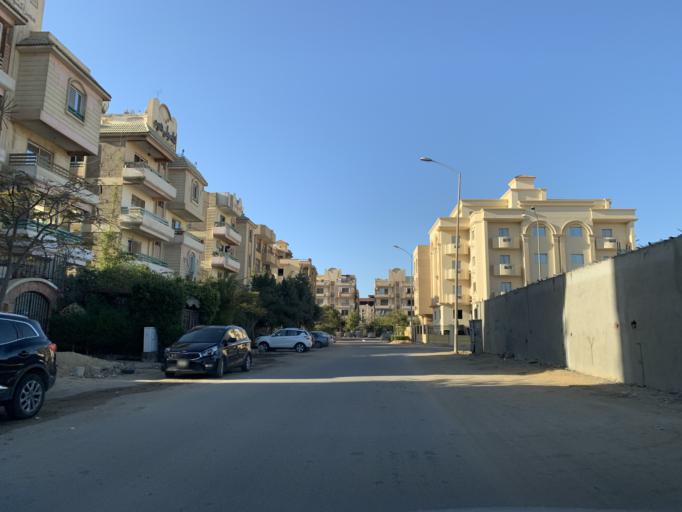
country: EG
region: Al Jizah
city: Madinat Sittah Uktubar
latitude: 29.9766
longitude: 30.9387
